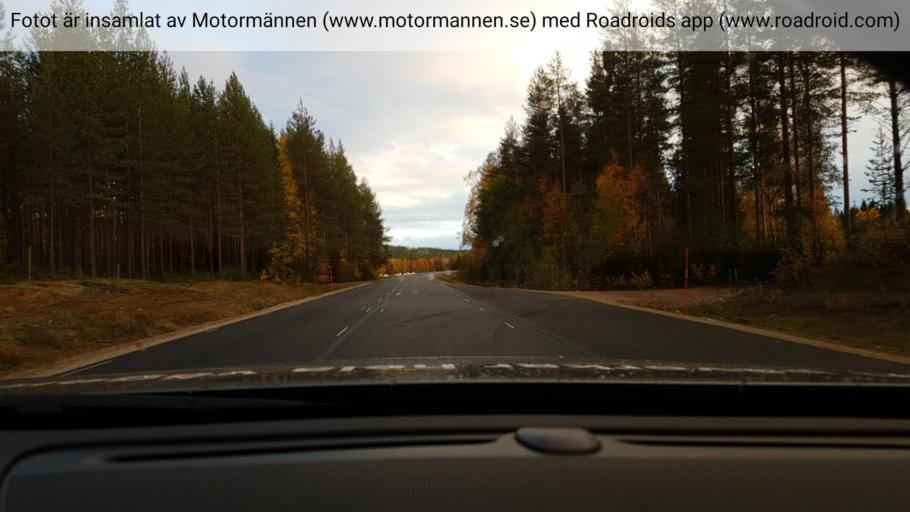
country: SE
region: Norrbotten
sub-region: Overkalix Kommun
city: OEverkalix
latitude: 66.4212
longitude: 22.8011
